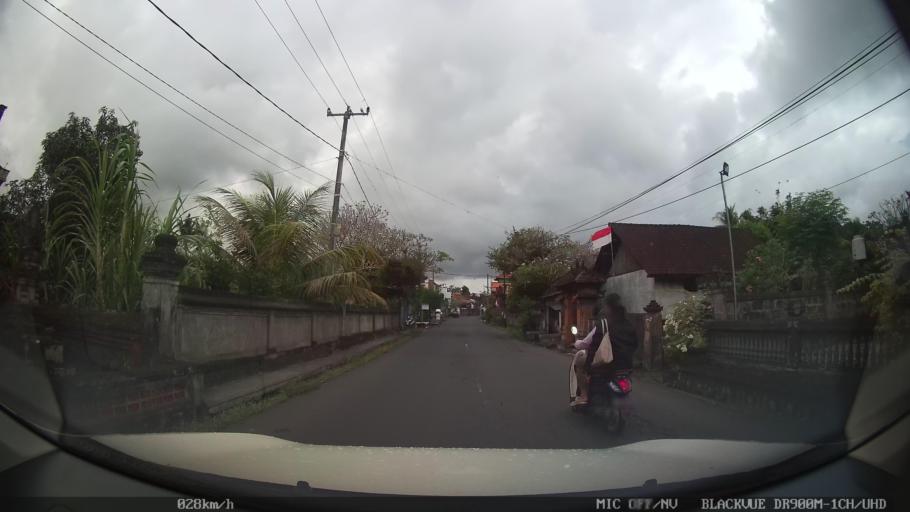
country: ID
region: Bali
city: Banjar Cemenggon
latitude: -8.5552
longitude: 115.1908
